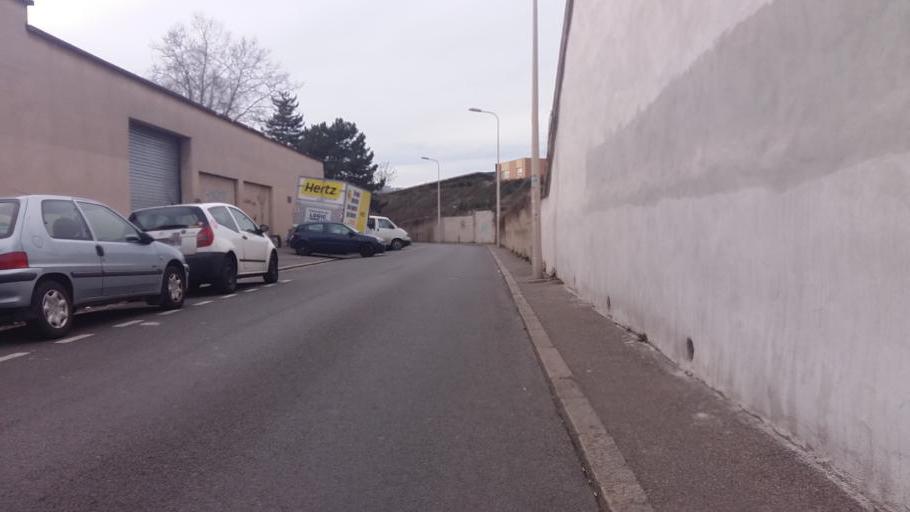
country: FR
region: Rhone-Alpes
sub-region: Departement du Rhone
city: Lyon
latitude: 45.7439
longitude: 4.8407
